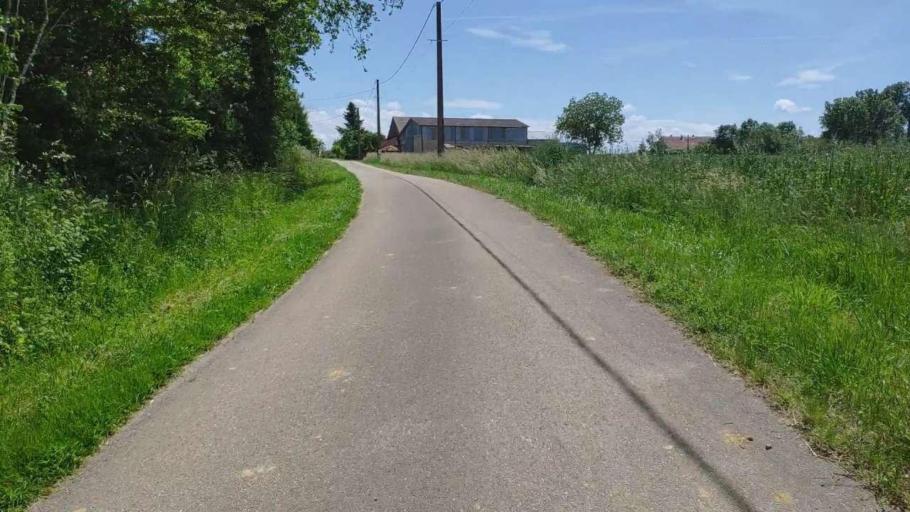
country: FR
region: Franche-Comte
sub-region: Departement du Jura
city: Bletterans
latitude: 46.7992
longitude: 5.3940
